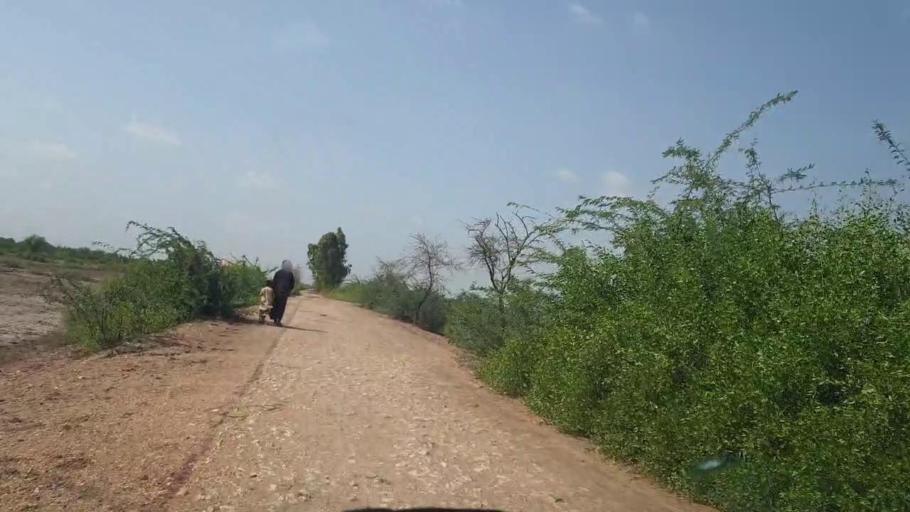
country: PK
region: Sindh
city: Berani
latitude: 25.7349
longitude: 68.9545
